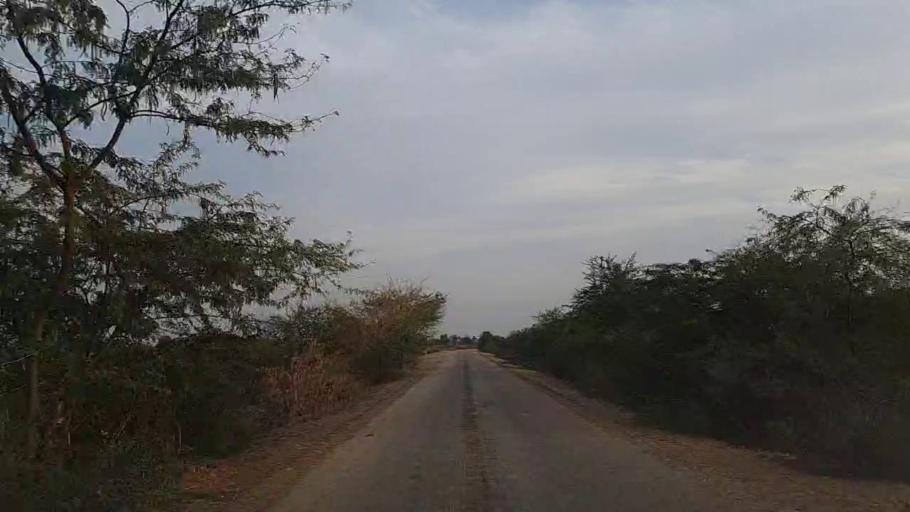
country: PK
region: Sindh
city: Jam Sahib
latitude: 26.4792
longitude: 68.5633
